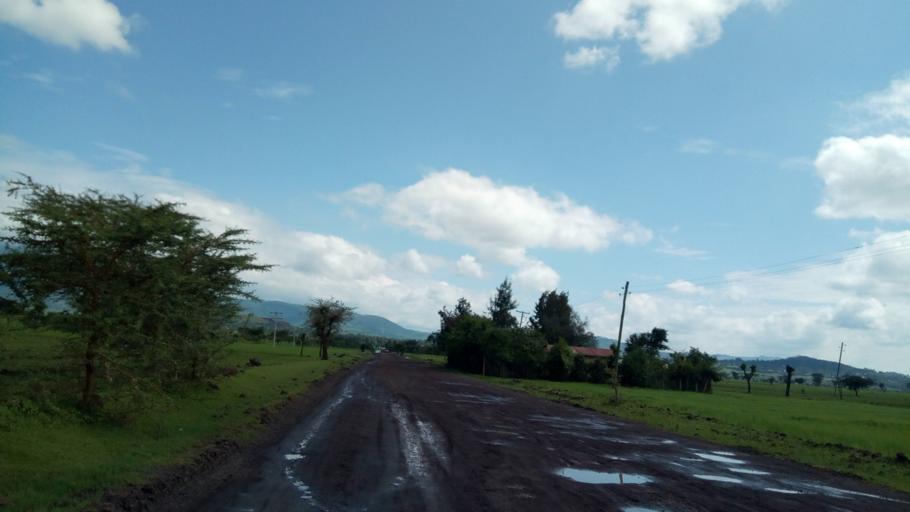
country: ET
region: Oromiya
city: Bishoftu
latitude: 8.8109
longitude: 39.0044
